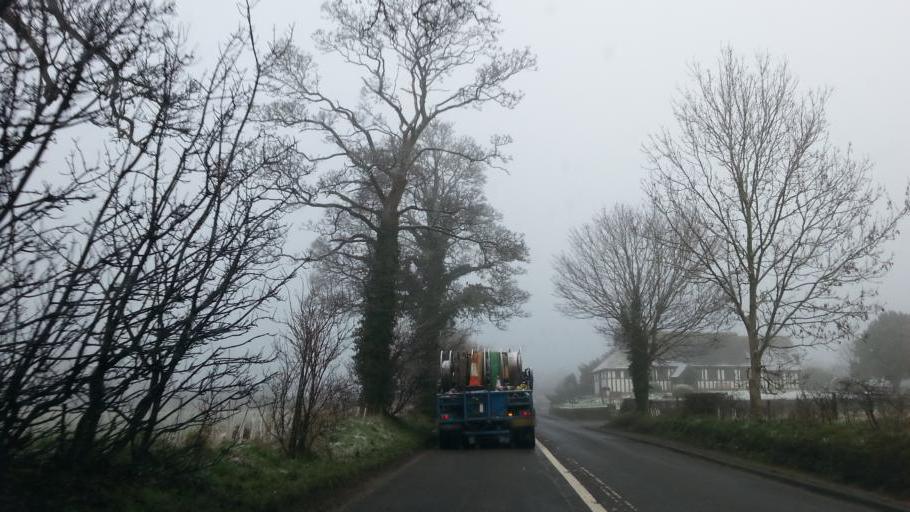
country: GB
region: England
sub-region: Cheshire East
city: Siddington
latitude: 53.2079
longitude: -2.2259
